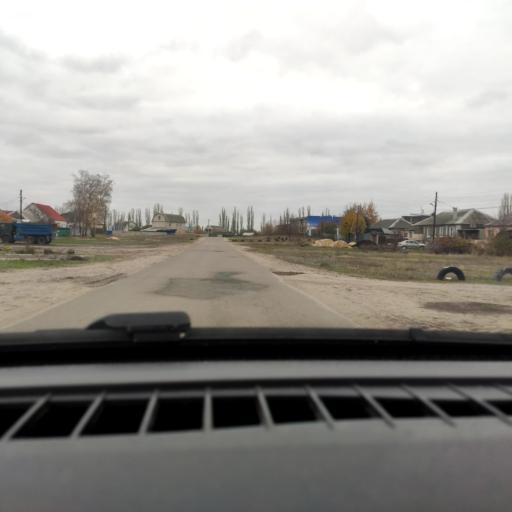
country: RU
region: Voronezj
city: Maslovka
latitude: 51.5789
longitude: 39.3036
